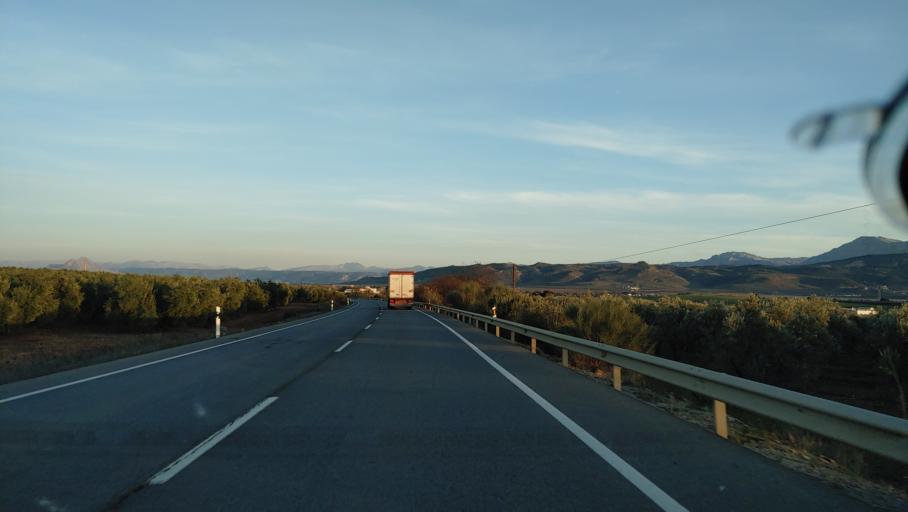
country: ES
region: Andalusia
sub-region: Provincia de Malaga
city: Humilladero
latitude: 37.0539
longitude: -4.6687
